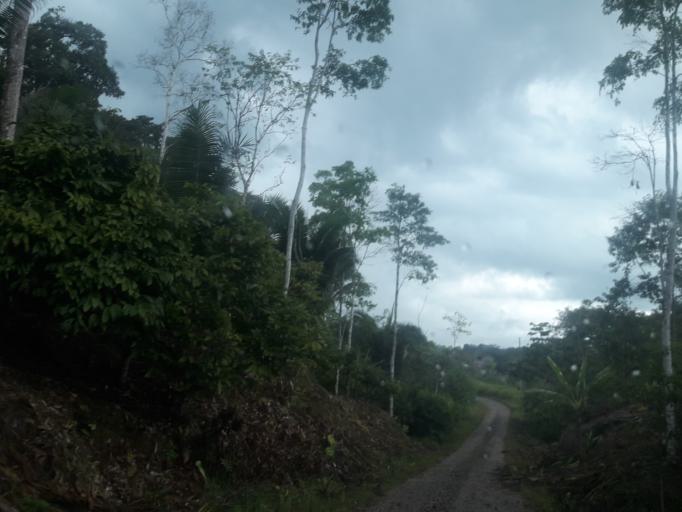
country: EC
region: Napo
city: Tena
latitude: -1.0863
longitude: -77.7087
